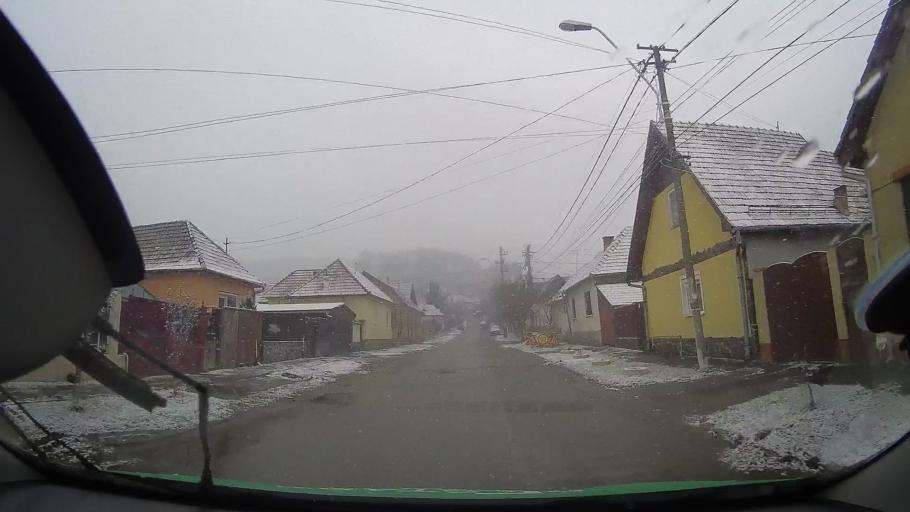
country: RO
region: Sibiu
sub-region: Municipiul Medias
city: Medias
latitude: 46.1631
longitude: 24.3636
